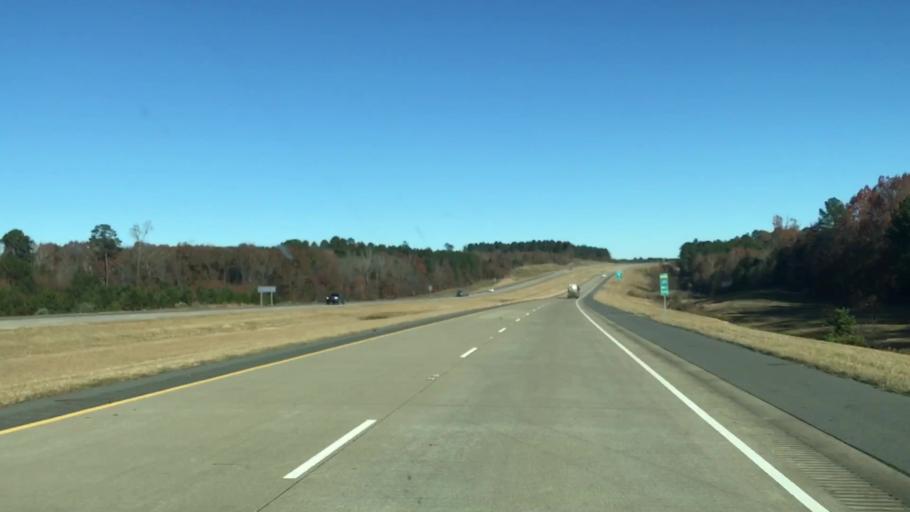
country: US
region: Louisiana
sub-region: Caddo Parish
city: Vivian
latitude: 32.9812
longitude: -93.9101
